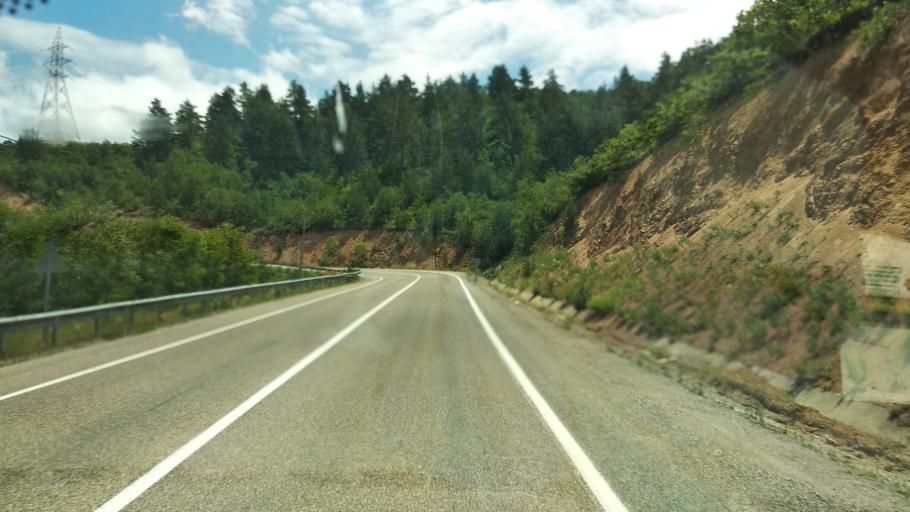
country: TR
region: Gumushane
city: Kose
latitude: 40.2983
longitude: 39.5689
